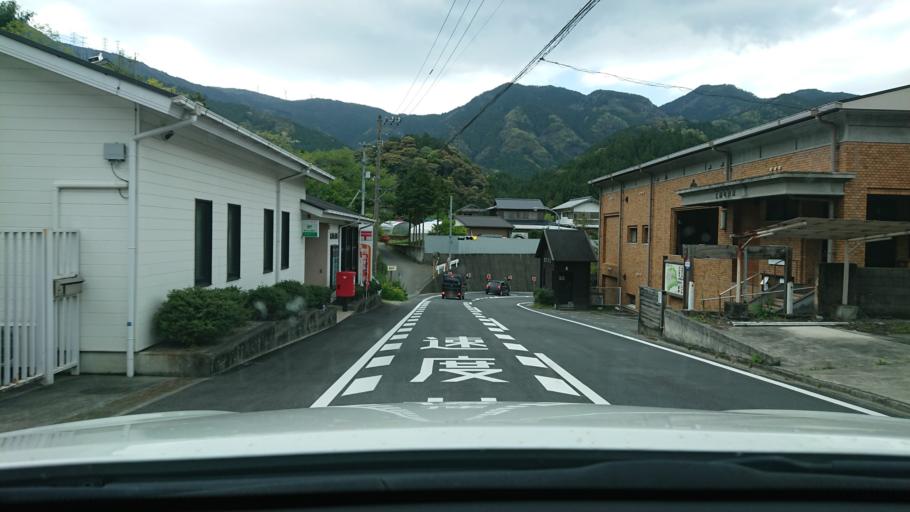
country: JP
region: Tokushima
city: Ishii
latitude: 33.9200
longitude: 134.4261
